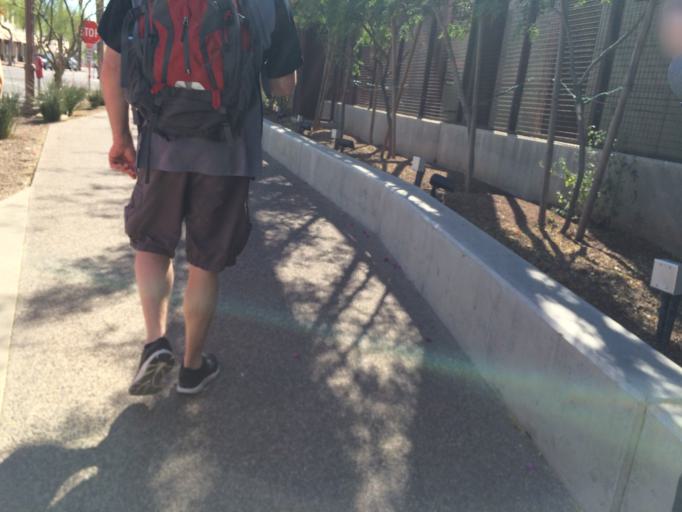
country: US
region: Arizona
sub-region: Maricopa County
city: Phoenix
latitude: 33.4504
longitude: -112.0681
